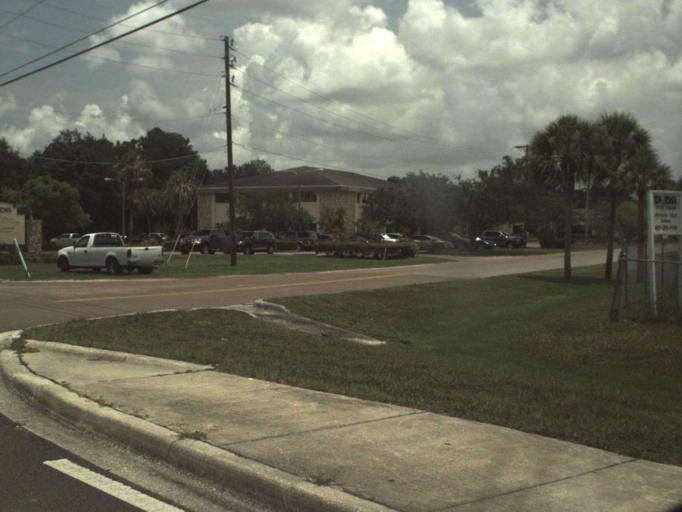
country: US
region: Florida
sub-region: Seminole County
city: Oviedo
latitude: 28.6517
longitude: -81.2285
